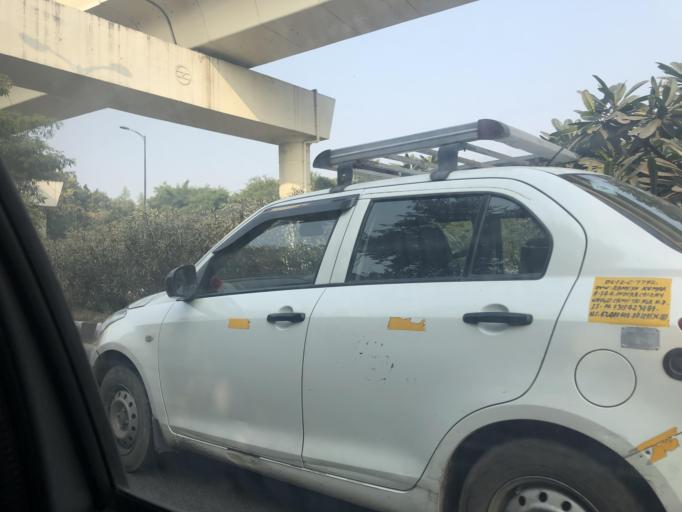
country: IN
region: NCT
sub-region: North West Delhi
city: Pitampura
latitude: 28.6742
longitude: 77.1362
